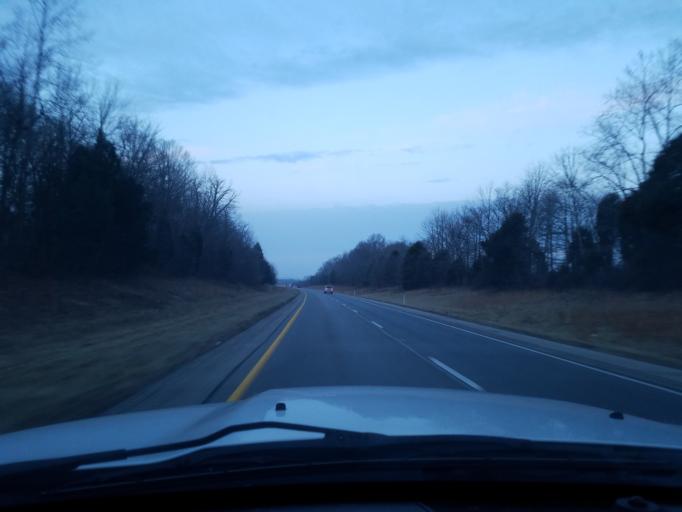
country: US
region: Indiana
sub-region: Harrison County
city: Corydon
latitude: 38.2513
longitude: -86.0534
